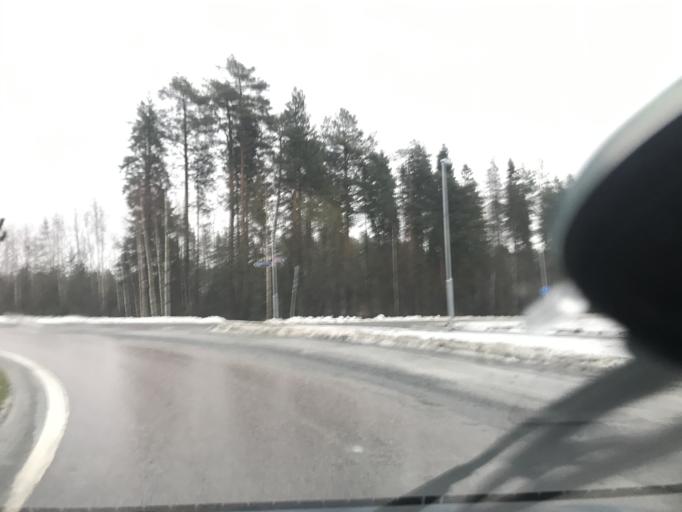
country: SE
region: Norrbotten
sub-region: Lulea Kommun
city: Gammelstad
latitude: 65.6331
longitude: 22.0330
